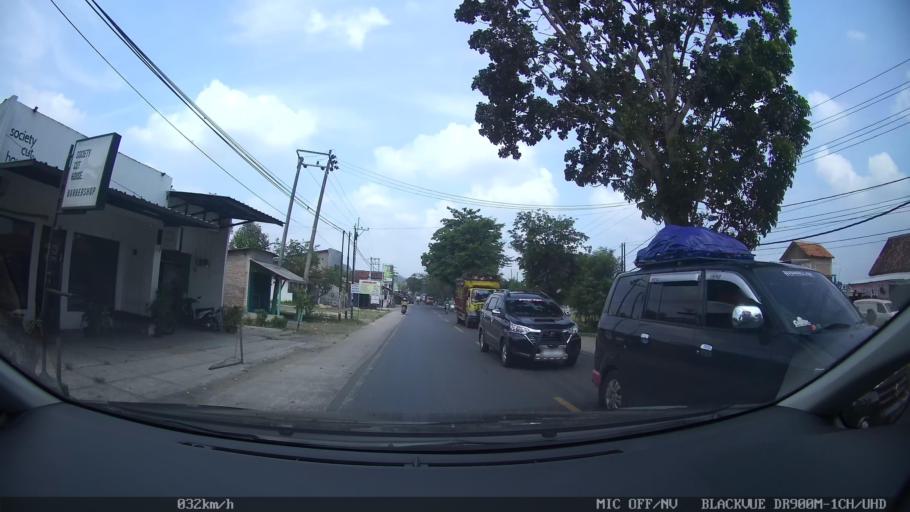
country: ID
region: Lampung
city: Pringsewu
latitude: -5.3564
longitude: 104.9636
